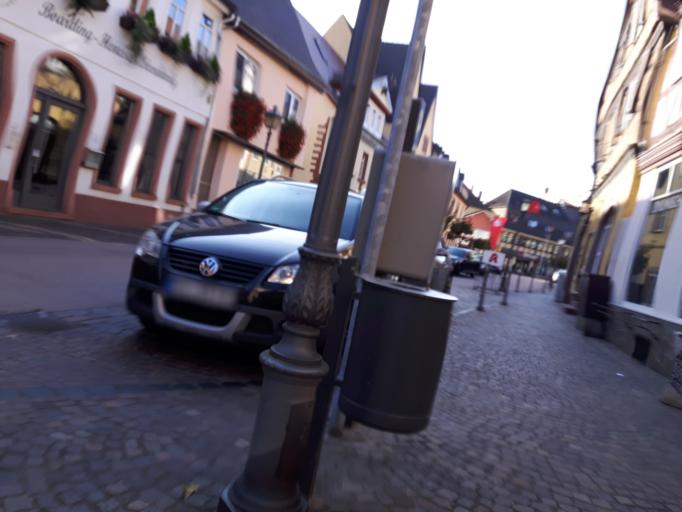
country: DE
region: Bavaria
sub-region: Regierungsbezirk Unterfranken
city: Obernburg am Main
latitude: 49.8411
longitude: 9.1469
